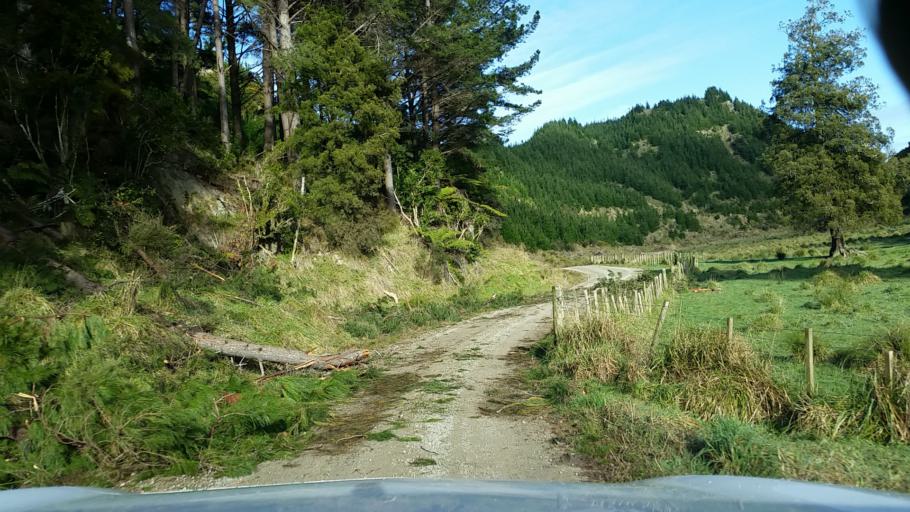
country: NZ
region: Taranaki
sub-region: South Taranaki District
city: Patea
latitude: -39.6911
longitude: 174.7600
